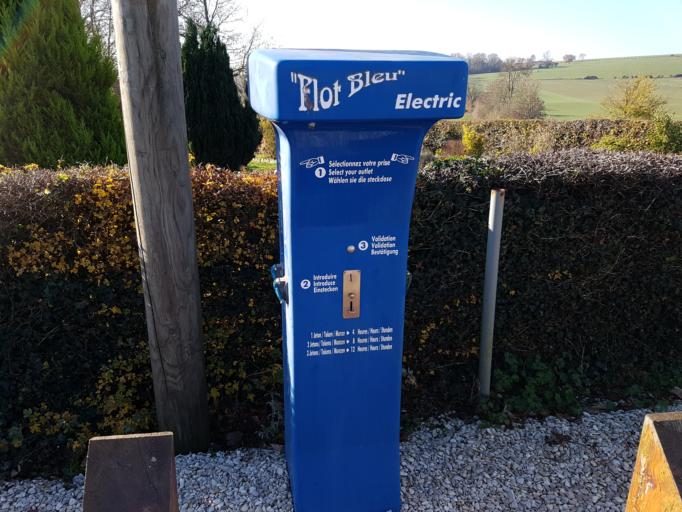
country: FR
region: Nord-Pas-de-Calais
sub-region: Departement du Pas-de-Calais
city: Beaurainville
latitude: 50.4939
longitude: 1.9647
